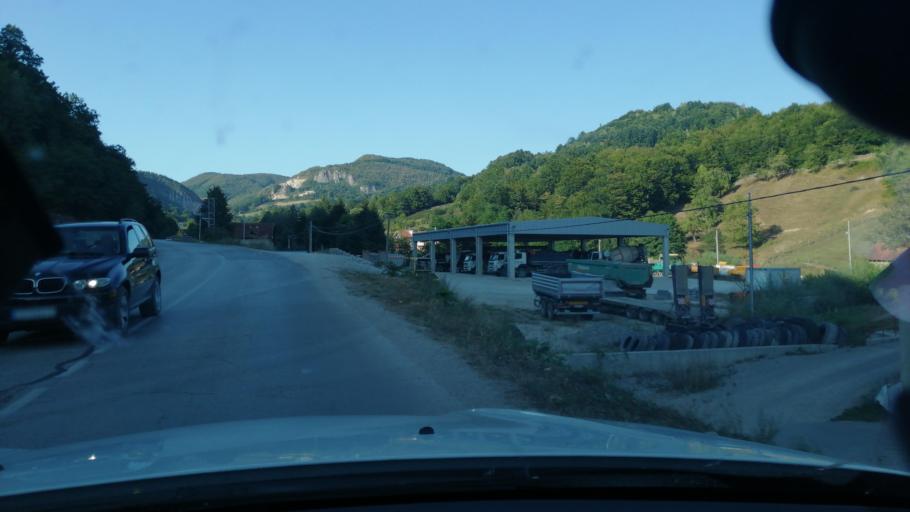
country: RS
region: Central Serbia
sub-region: Moravicki Okrug
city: Ivanjica
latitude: 43.6065
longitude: 20.2344
